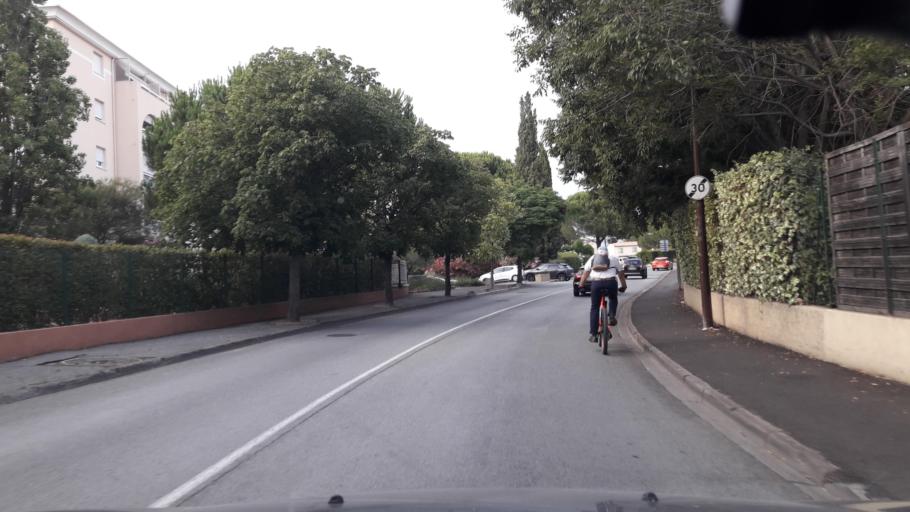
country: FR
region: Provence-Alpes-Cote d'Azur
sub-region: Departement du Var
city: Frejus
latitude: 43.4366
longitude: 6.7542
